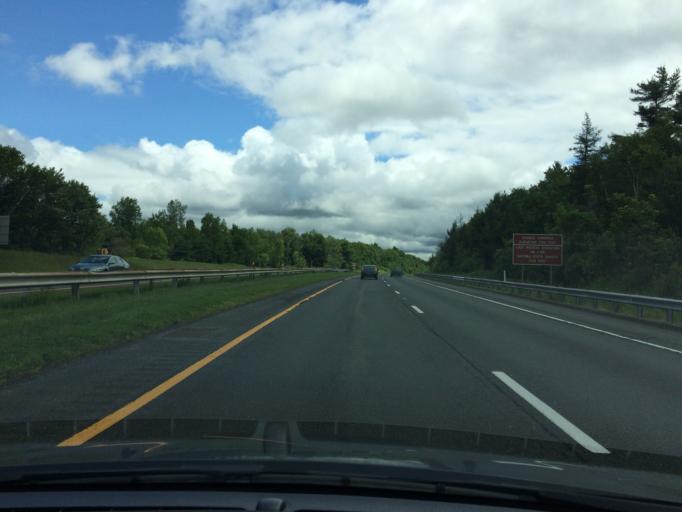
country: US
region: Massachusetts
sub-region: Berkshire County
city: Otis
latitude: 42.2449
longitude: -73.0797
